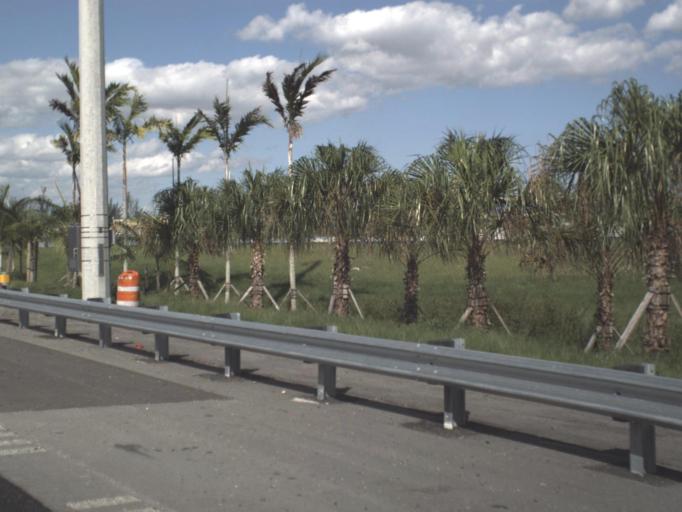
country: US
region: Florida
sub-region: Broward County
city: Broadview Park
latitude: 26.0858
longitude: -80.2160
